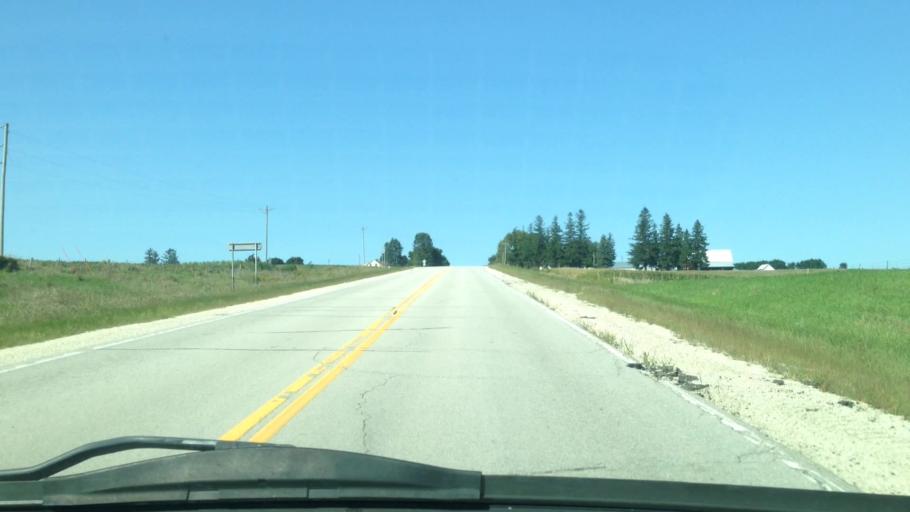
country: US
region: Minnesota
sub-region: Houston County
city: Spring Grove
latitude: 43.6043
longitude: -91.7901
